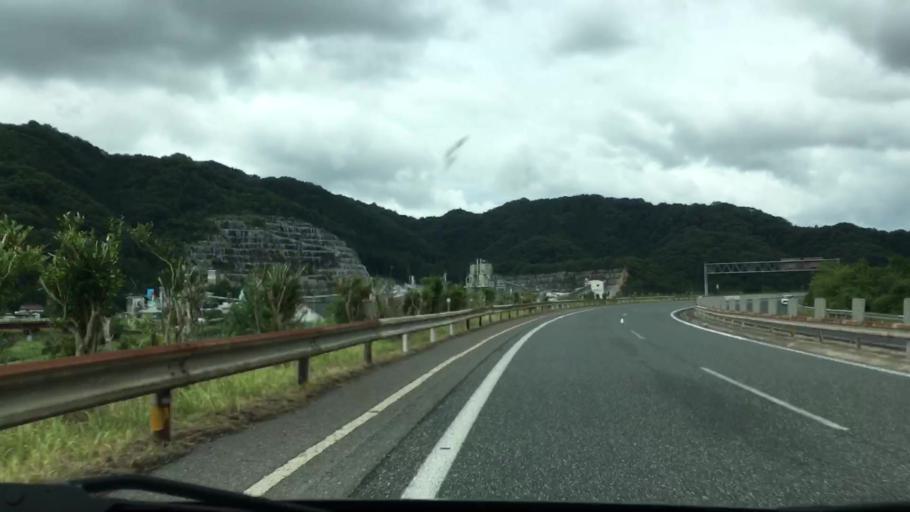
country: JP
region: Okayama
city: Takahashi
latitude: 34.9784
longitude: 133.6742
